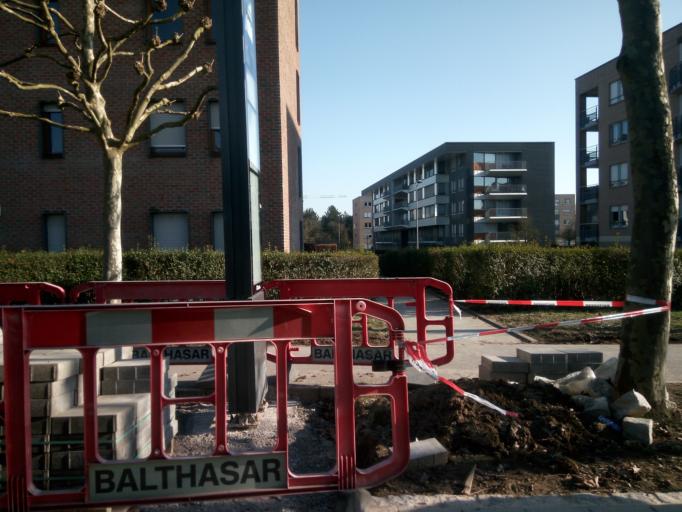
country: LU
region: Luxembourg
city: Kirchberg
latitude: 49.6325
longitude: 6.1614
